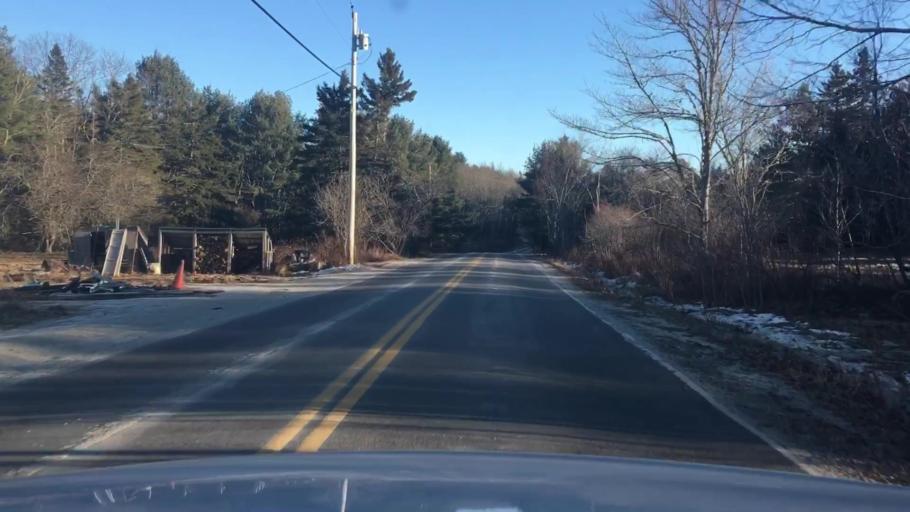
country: US
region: Maine
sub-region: Hancock County
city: Penobscot
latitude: 44.3887
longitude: -68.6987
